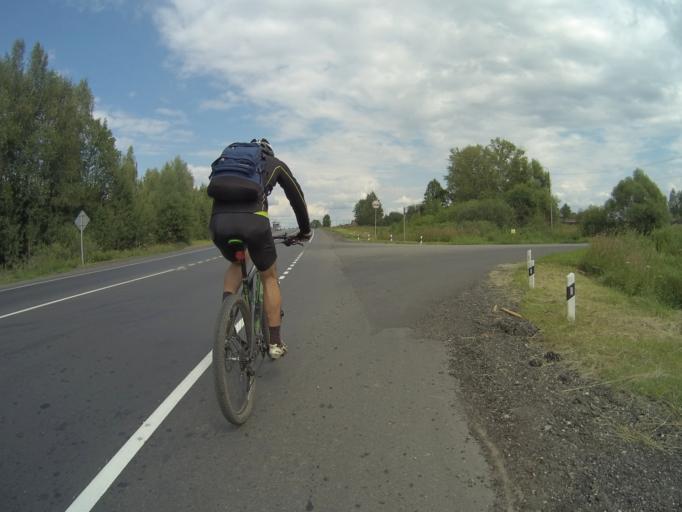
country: RU
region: Vladimir
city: Kideksha
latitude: 56.5006
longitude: 40.5376
